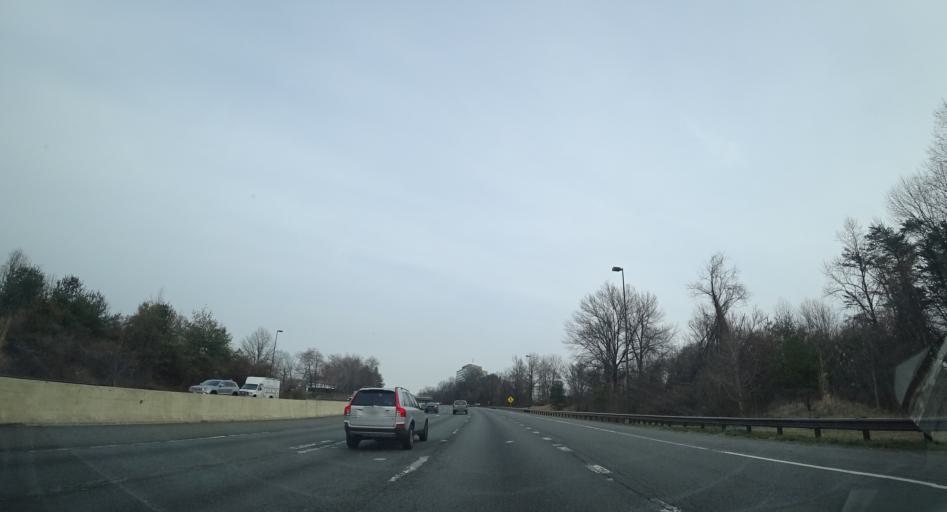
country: US
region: Maryland
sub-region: Montgomery County
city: North Bethesda
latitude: 39.0224
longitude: -77.1422
